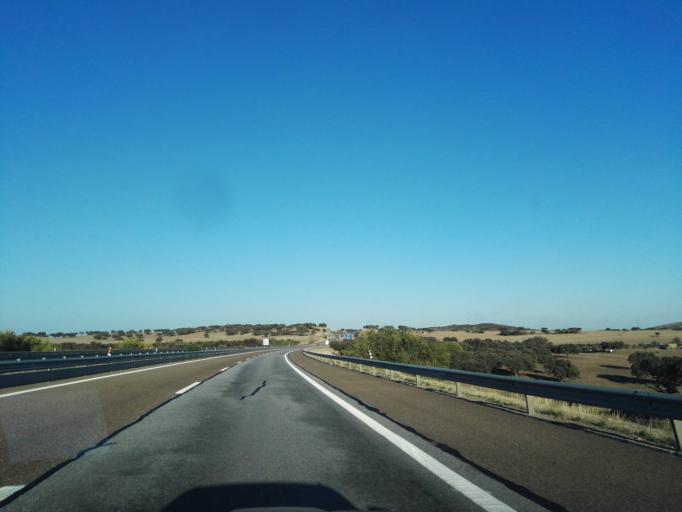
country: PT
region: Portalegre
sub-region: Elvas
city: Elvas
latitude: 38.9007
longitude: -7.2001
